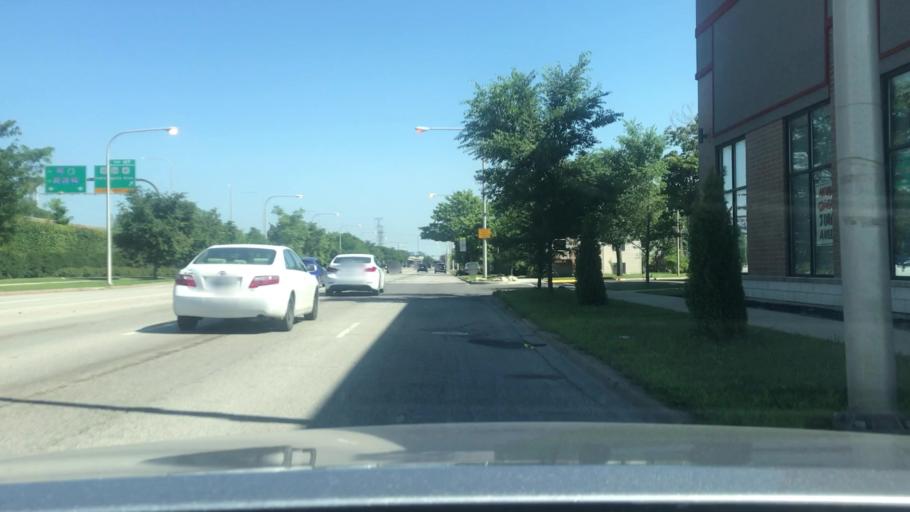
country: US
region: Indiana
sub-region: Lake County
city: Whiting
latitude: 41.7096
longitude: -87.5319
